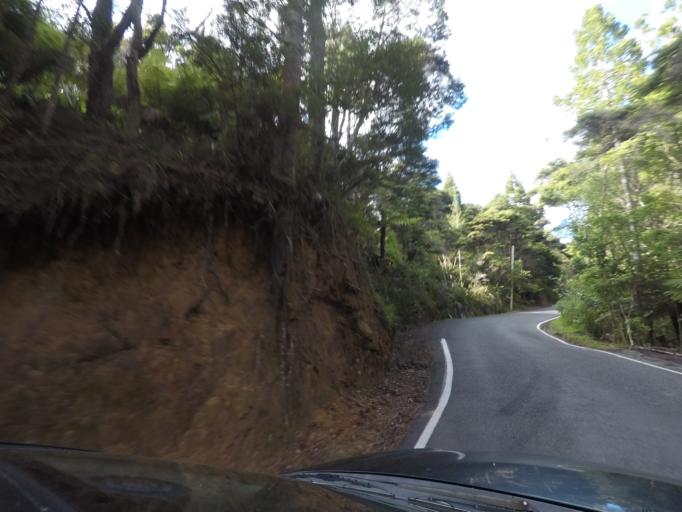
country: NZ
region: Auckland
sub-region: Auckland
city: Titirangi
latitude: -37.0169
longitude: 174.5521
